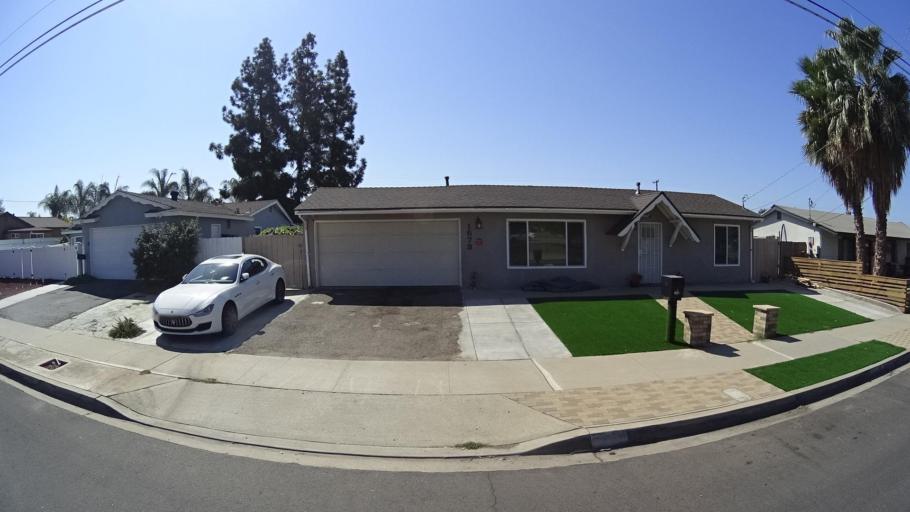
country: US
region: California
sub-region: San Diego County
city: Bostonia
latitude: 32.7928
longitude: -116.9237
